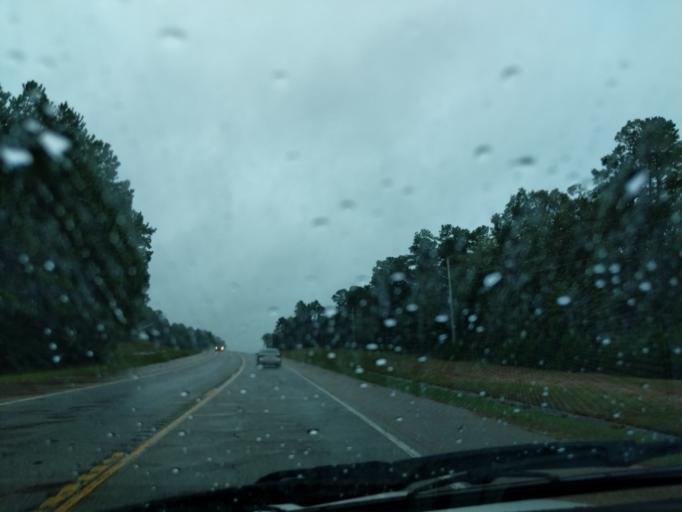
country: US
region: Louisiana
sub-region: Webster Parish
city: Minden
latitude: 32.5965
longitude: -93.2495
